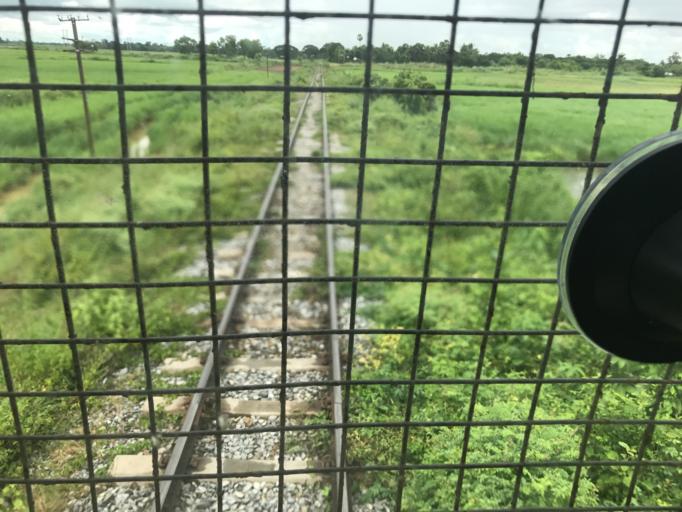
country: MM
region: Bago
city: Paungde
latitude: 18.6755
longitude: 95.4048
